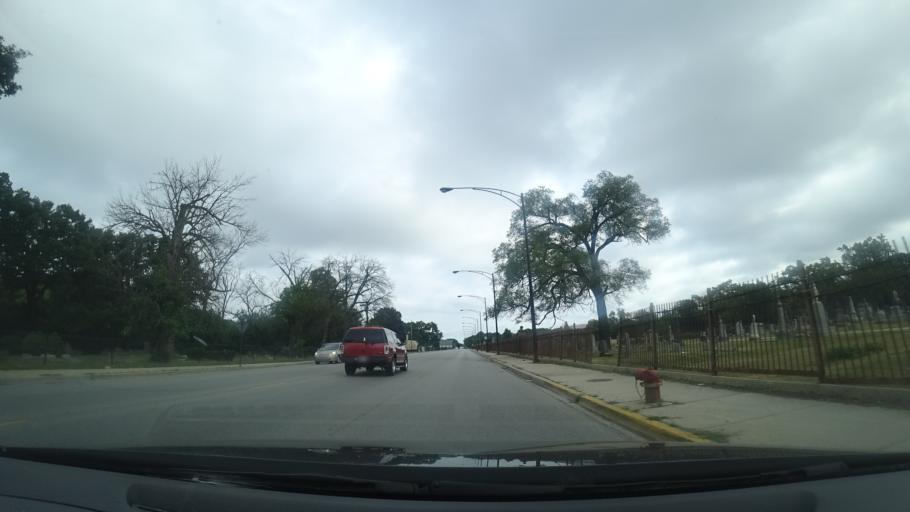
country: US
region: Illinois
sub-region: Cook County
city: Lincolnwood
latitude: 41.9785
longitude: -87.7282
